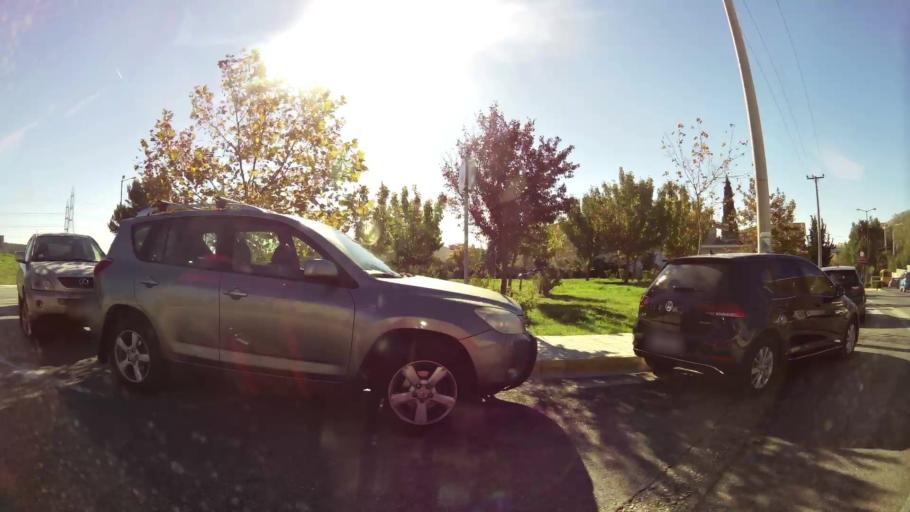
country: GR
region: Attica
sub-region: Nomarchia Anatolikis Attikis
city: Gerakas
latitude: 38.0126
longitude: 23.8602
